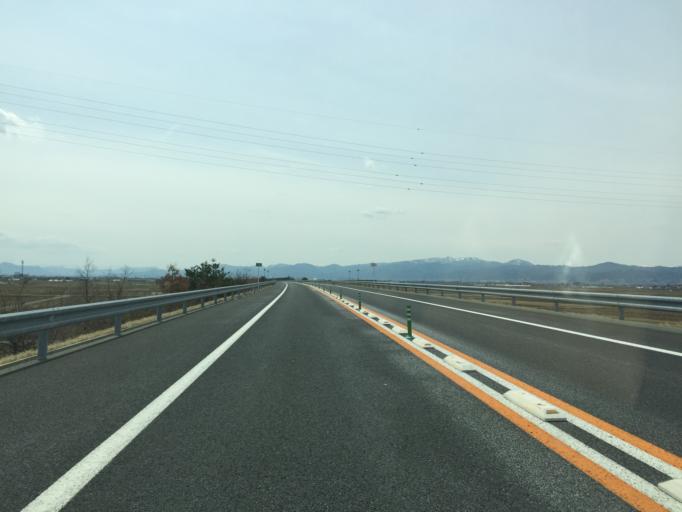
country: JP
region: Yamagata
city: Tendo
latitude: 38.3517
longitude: 140.3394
